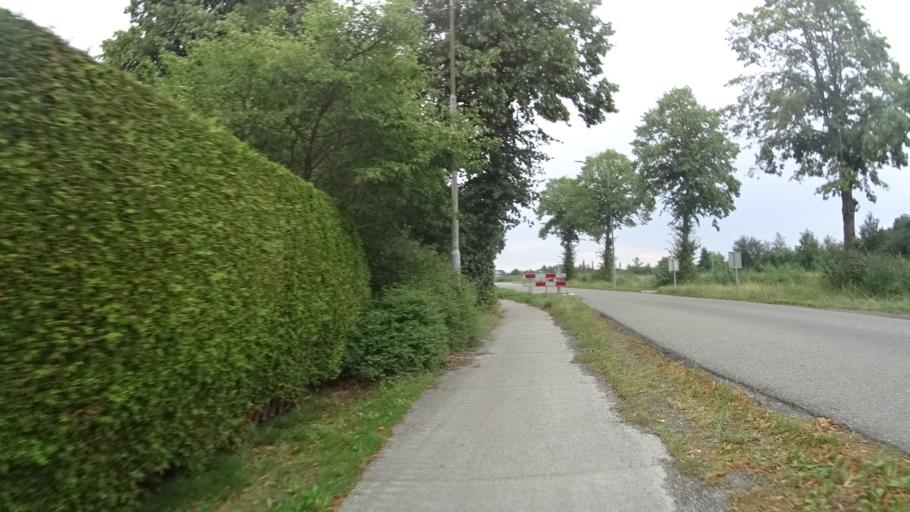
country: NL
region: Groningen
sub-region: Gemeente Hoogezand-Sappemeer
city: Hoogezand
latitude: 53.2354
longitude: 6.7123
